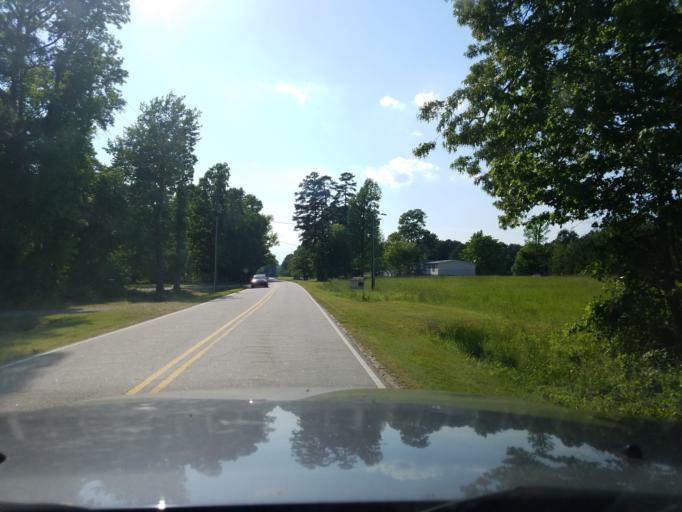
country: US
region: North Carolina
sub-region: Vance County
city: Henderson
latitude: 36.4068
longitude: -78.3704
